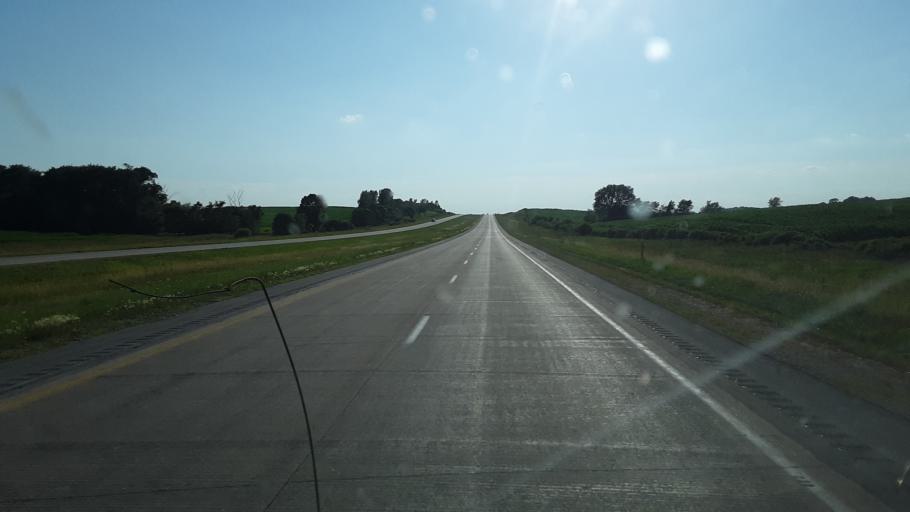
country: US
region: Iowa
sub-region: Hardin County
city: Iowa Falls
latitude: 42.4484
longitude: -93.3069
